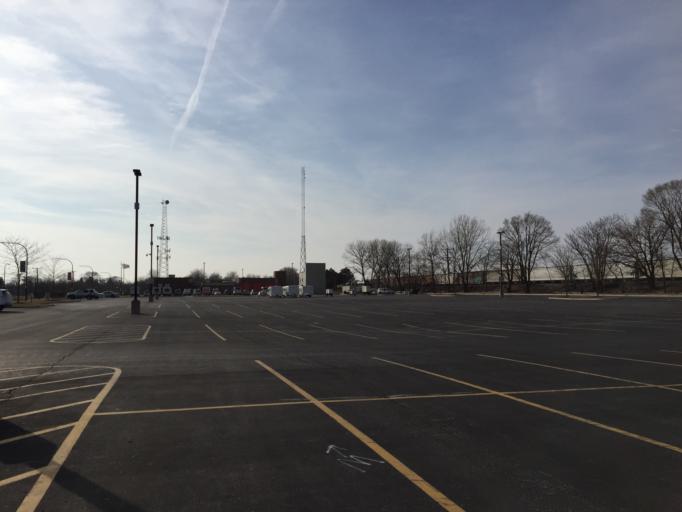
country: US
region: Illinois
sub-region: Cook County
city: Cicero
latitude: 41.8313
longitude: -87.7563
